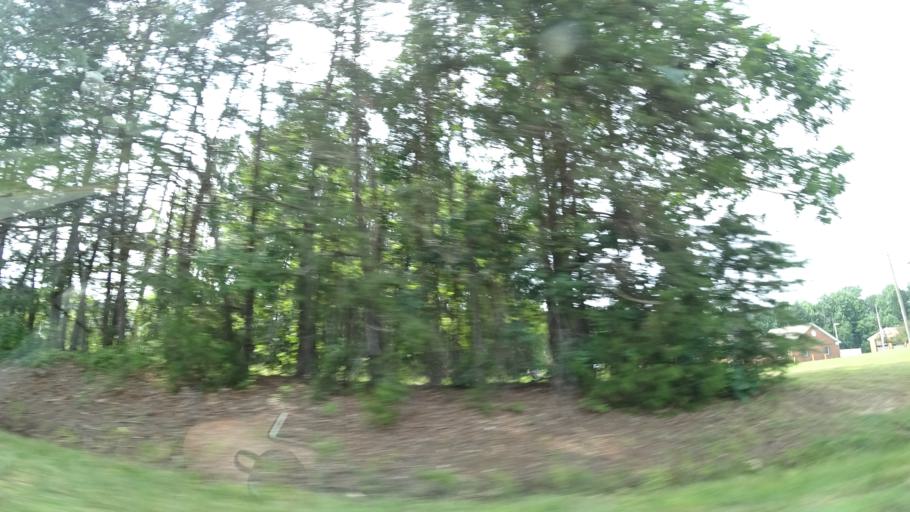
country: US
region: Virginia
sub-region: Spotsylvania County
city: Spotsylvania Courthouse
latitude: 38.1247
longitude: -77.7391
